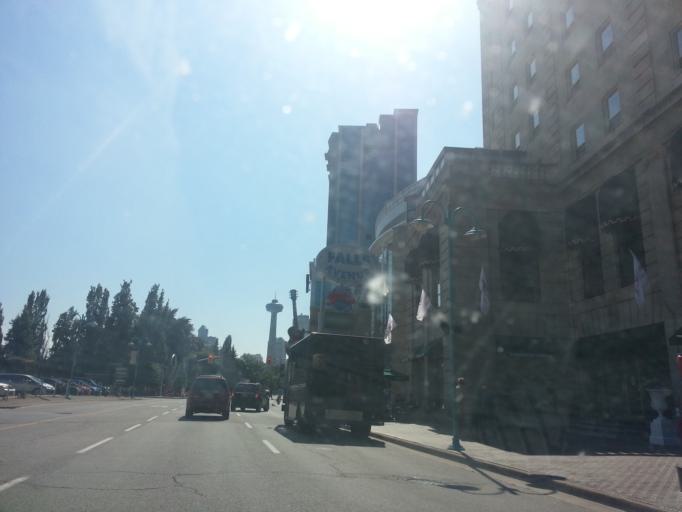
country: CA
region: Ontario
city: Niagara Falls
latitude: 43.0919
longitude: -79.0712
